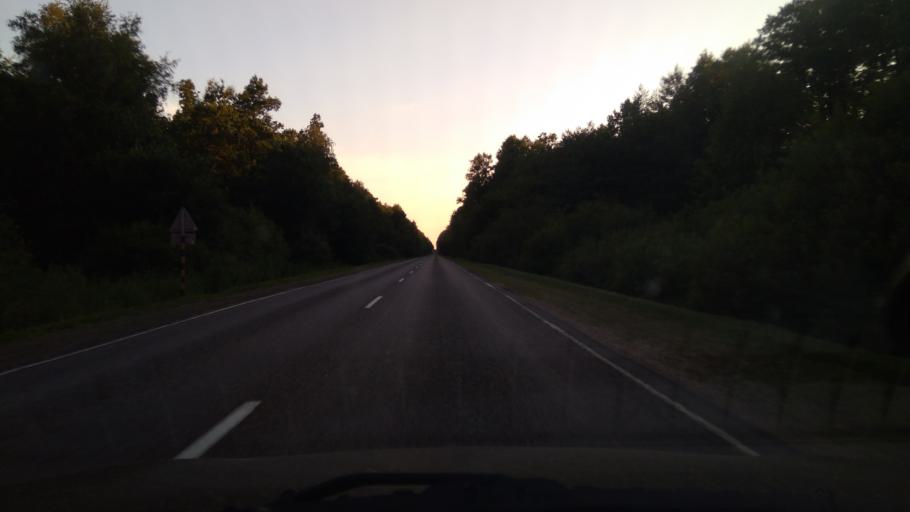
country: BY
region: Brest
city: Nyakhachava
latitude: 52.6115
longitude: 25.1398
